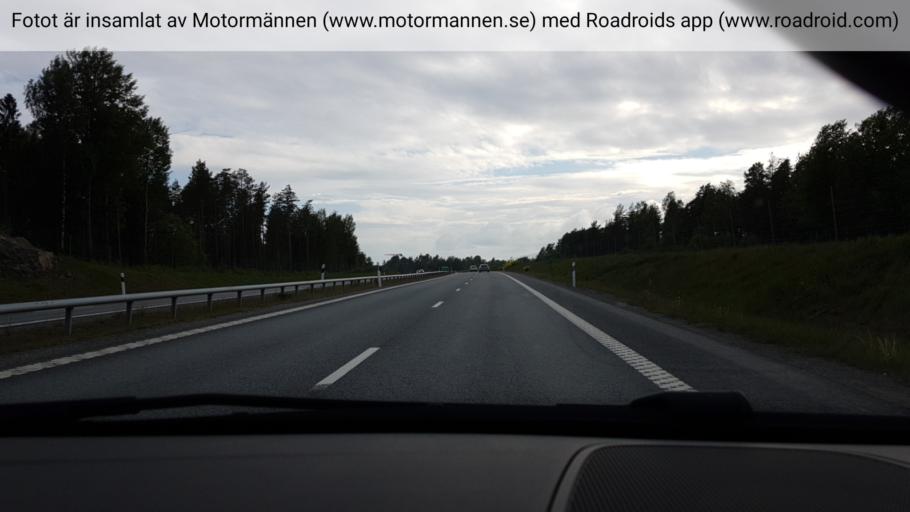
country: SE
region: Stockholm
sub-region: Haninge Kommun
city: Jordbro
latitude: 59.0913
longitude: 18.0932
